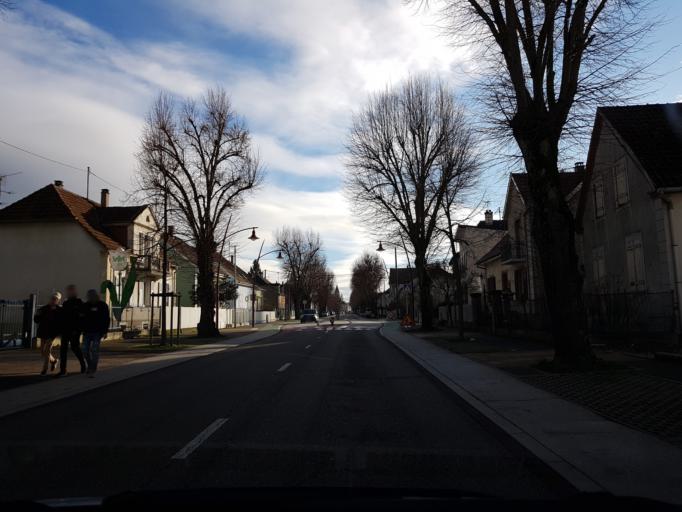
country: FR
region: Alsace
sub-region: Departement du Haut-Rhin
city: Habsheim
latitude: 47.7352
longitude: 7.4172
